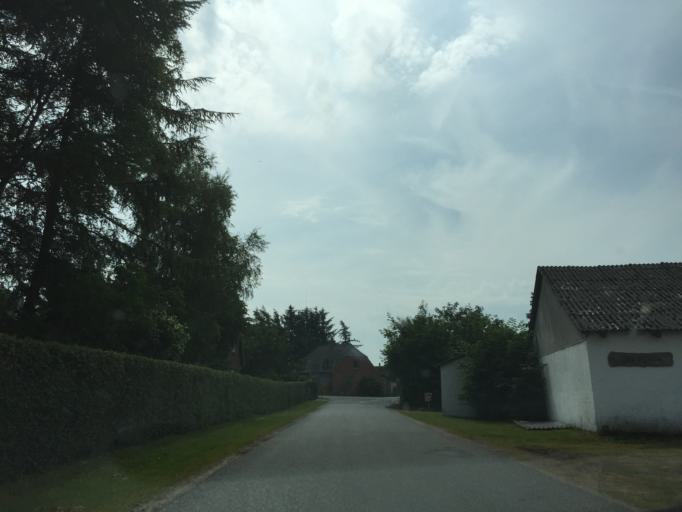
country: DK
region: Central Jutland
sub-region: Silkeborg Kommune
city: Virklund
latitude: 56.0923
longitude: 9.4701
